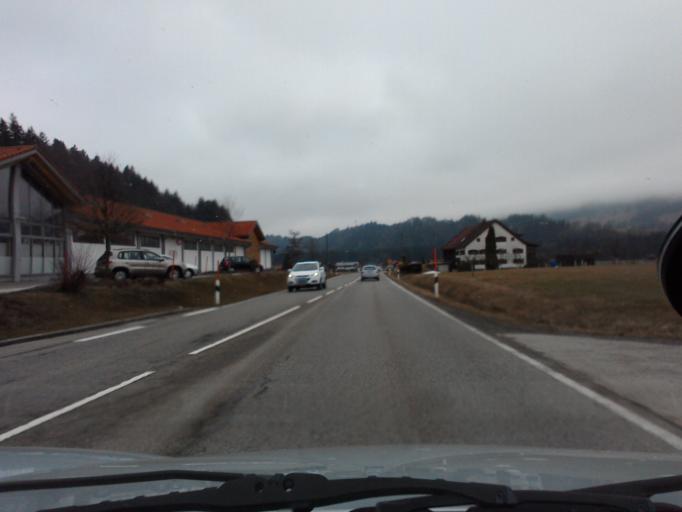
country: DE
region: Bavaria
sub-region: Swabia
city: Oberstdorf
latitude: 47.4319
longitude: 10.2697
